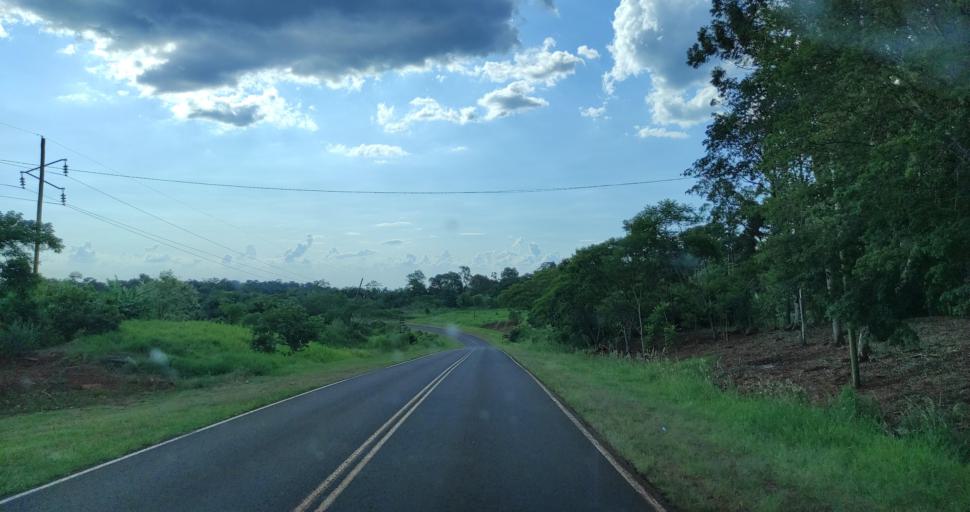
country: AR
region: Misiones
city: San Vicente
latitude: -26.3375
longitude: -54.1715
